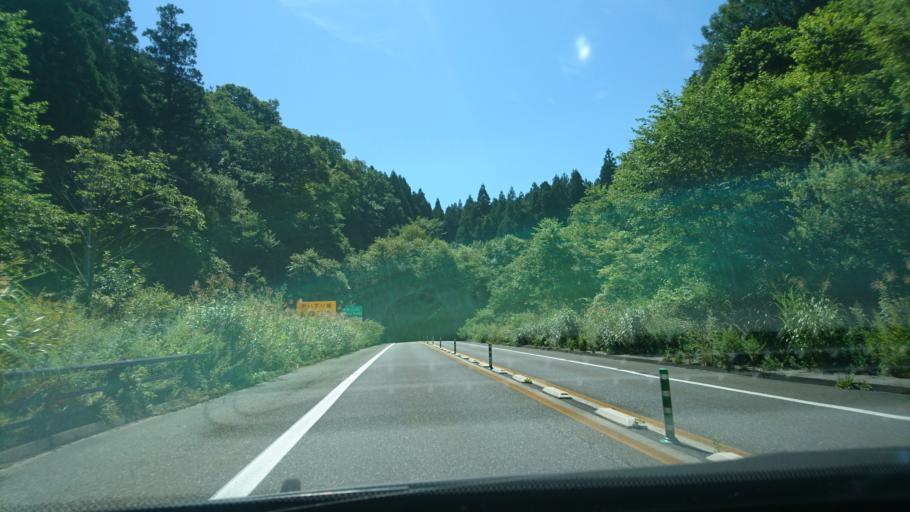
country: JP
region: Iwate
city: Tono
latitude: 39.2560
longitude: 141.6282
